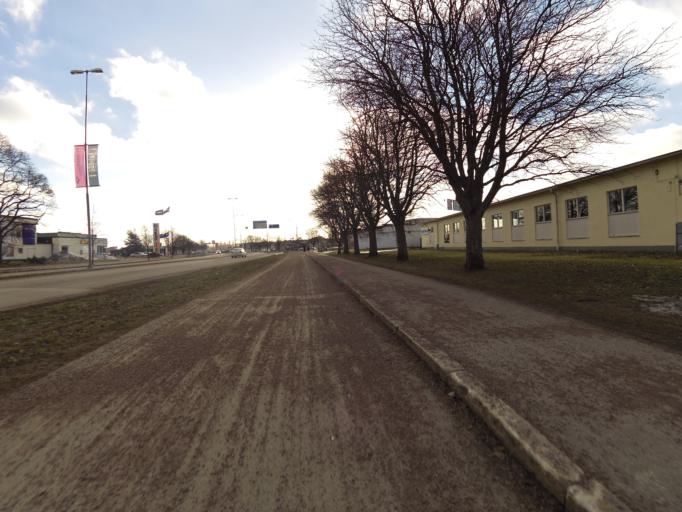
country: SE
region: Gaevleborg
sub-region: Gavle Kommun
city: Gavle
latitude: 60.6625
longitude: 17.1561
